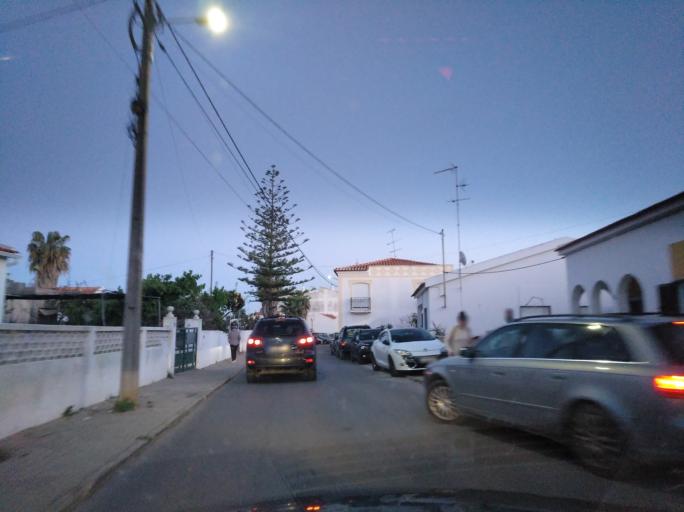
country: PT
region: Faro
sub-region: Vila Real de Santo Antonio
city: Monte Gordo
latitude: 37.1817
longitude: -7.5044
